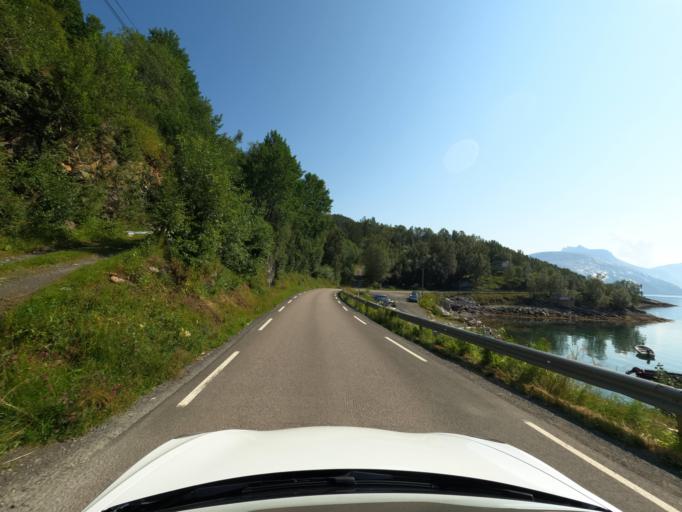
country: NO
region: Nordland
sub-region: Narvik
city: Narvik
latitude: 68.2963
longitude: 17.3555
